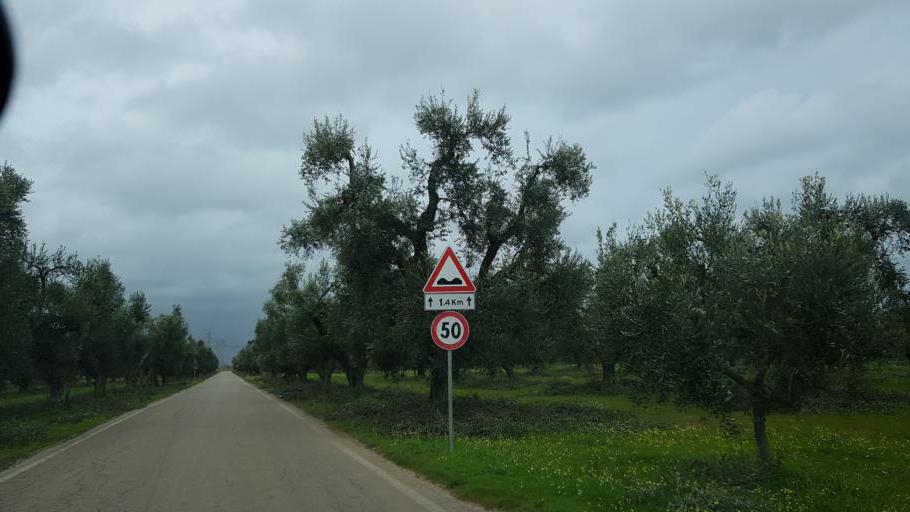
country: IT
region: Apulia
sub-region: Provincia di Brindisi
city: Brindisi
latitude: 40.5958
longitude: 17.9003
